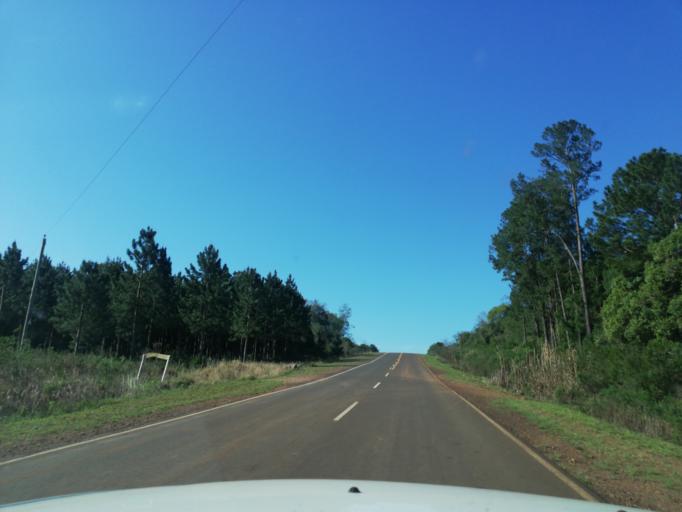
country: AR
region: Misiones
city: Arroyo del Medio
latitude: -27.6908
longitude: -55.3998
